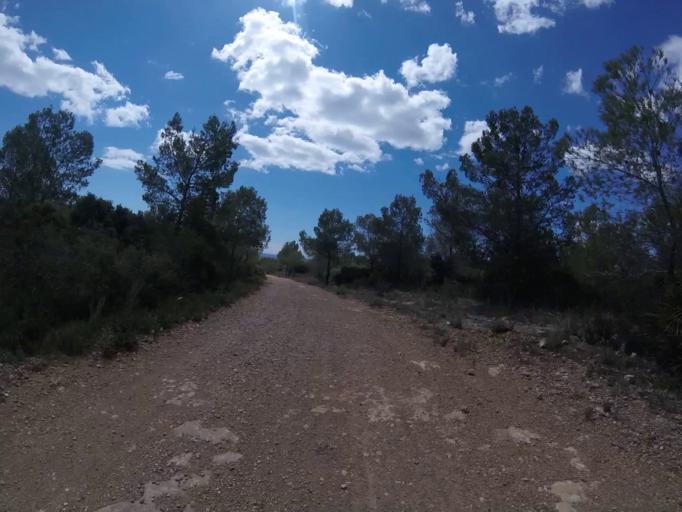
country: ES
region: Valencia
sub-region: Provincia de Castello
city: Alcoceber
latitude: 40.2908
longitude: 0.3162
